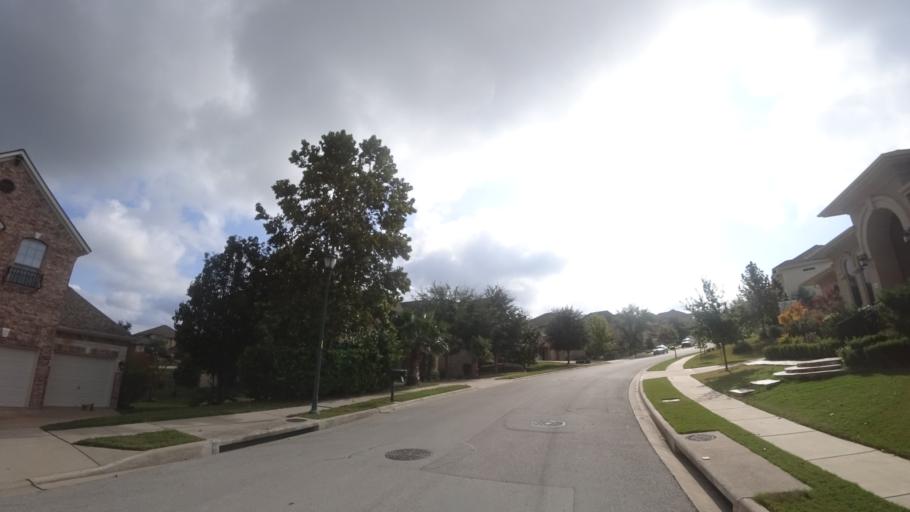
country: US
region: Texas
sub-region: Travis County
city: Barton Creek
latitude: 30.3161
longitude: -97.9009
